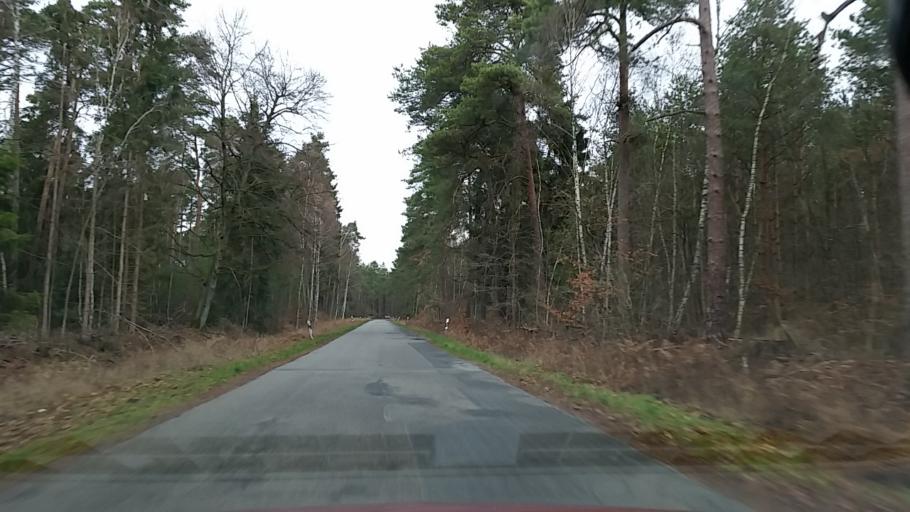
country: DE
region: Lower Saxony
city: Luder
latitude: 52.7754
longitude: 10.6692
